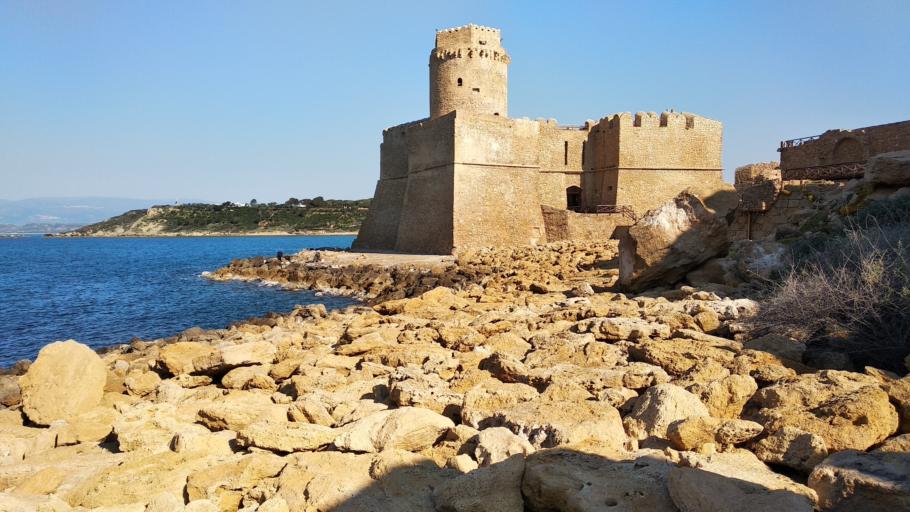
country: IT
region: Calabria
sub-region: Provincia di Crotone
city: Le Castella
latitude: 38.9061
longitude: 17.0216
